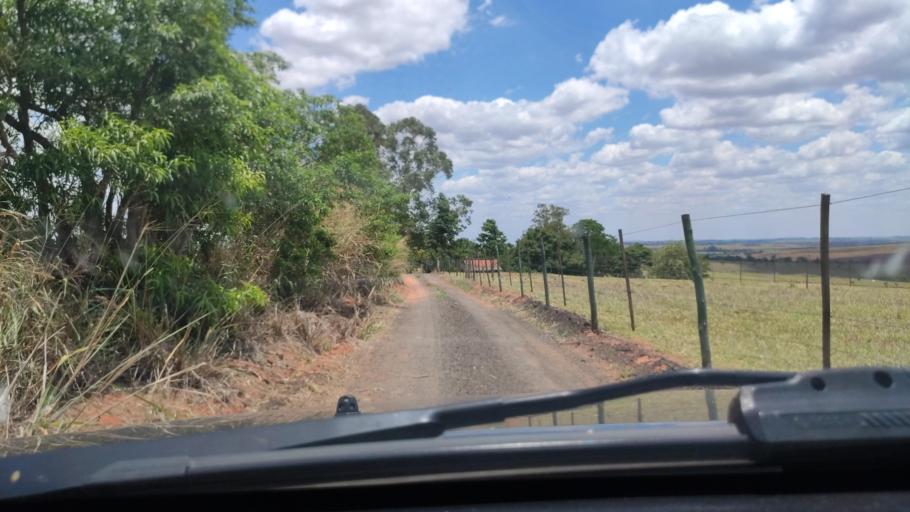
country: BR
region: Sao Paulo
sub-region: Duartina
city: Duartina
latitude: -22.6537
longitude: -49.4096
